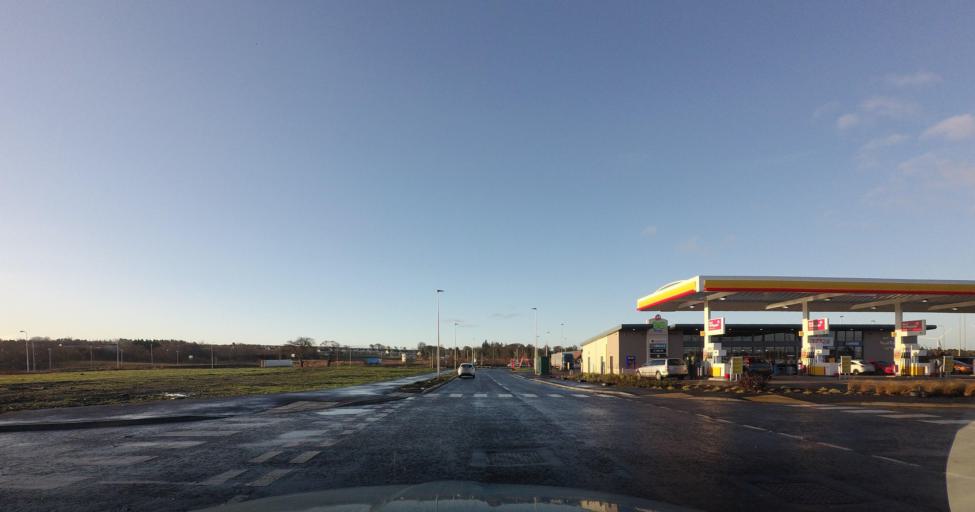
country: GB
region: Scotland
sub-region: West Lothian
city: Armadale
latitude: 55.8687
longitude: -3.7022
